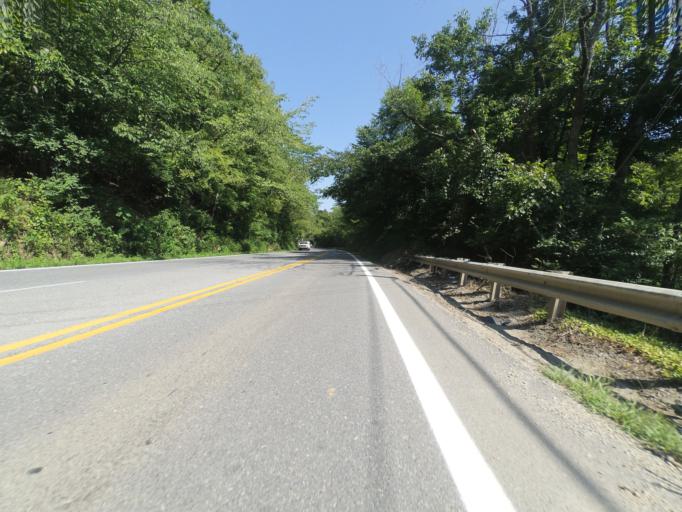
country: US
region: West Virginia
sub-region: Wayne County
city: Lavalette
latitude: 38.3660
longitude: -82.4536
